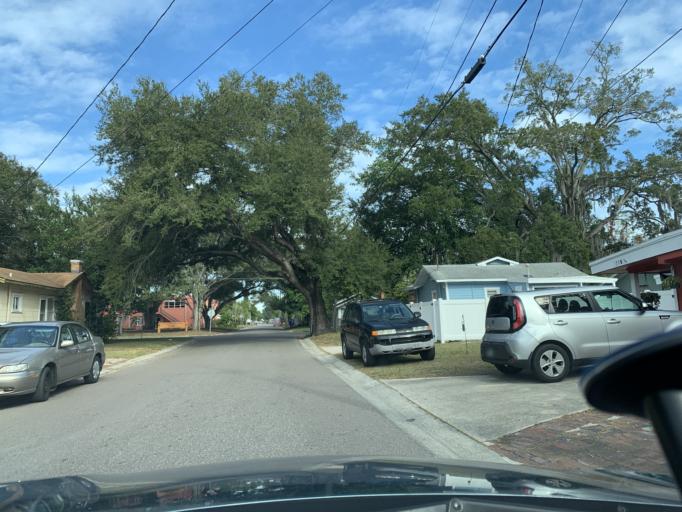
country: US
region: Florida
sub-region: Pinellas County
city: Lealman
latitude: 27.7971
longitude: -82.6581
